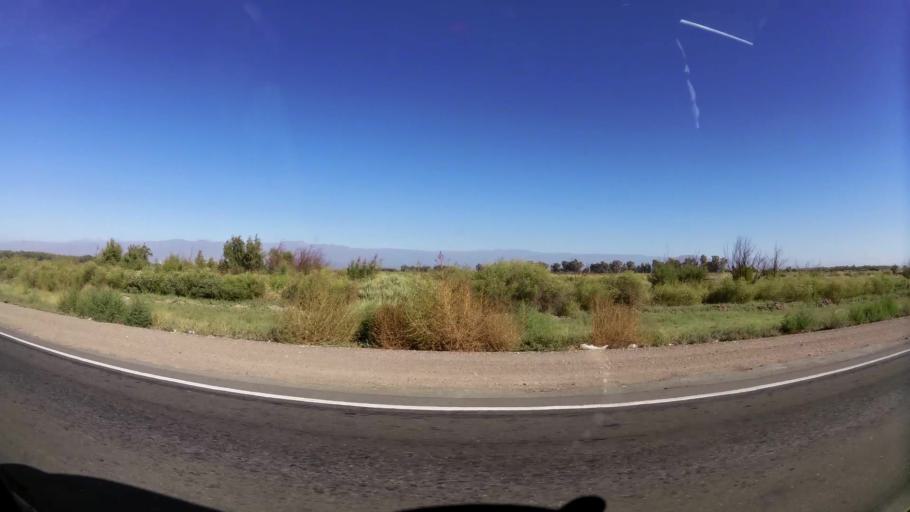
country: AR
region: Mendoza
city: General Lavalle
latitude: -32.7151
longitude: -68.6796
